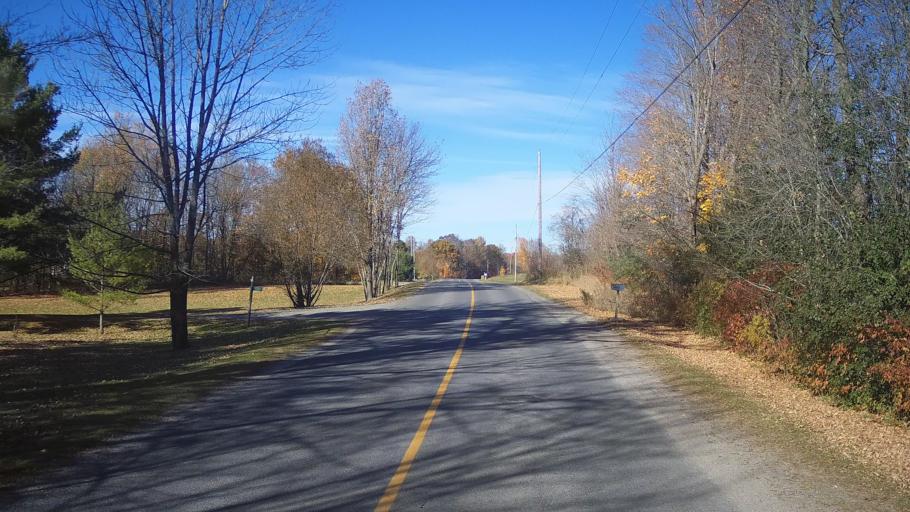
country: CA
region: Ontario
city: Kingston
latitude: 44.4392
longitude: -76.5231
